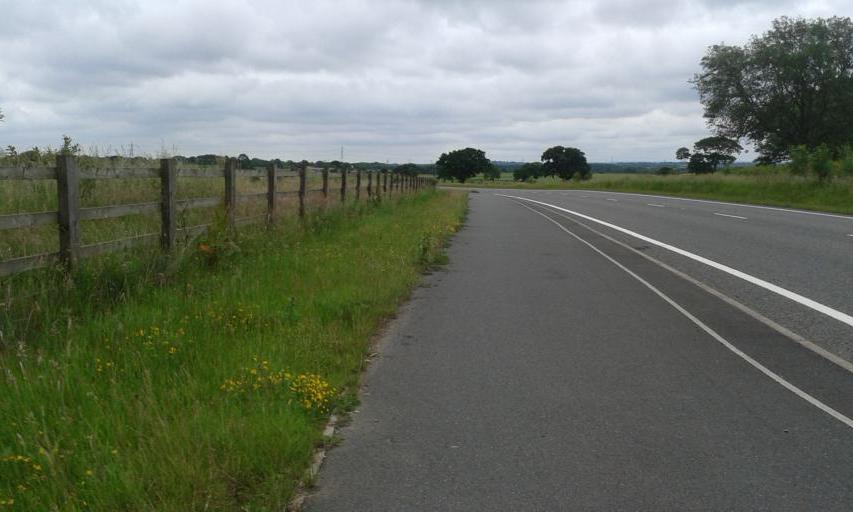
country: GB
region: England
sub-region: Leicestershire
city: Earl Shilton
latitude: 52.5694
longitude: -1.3014
